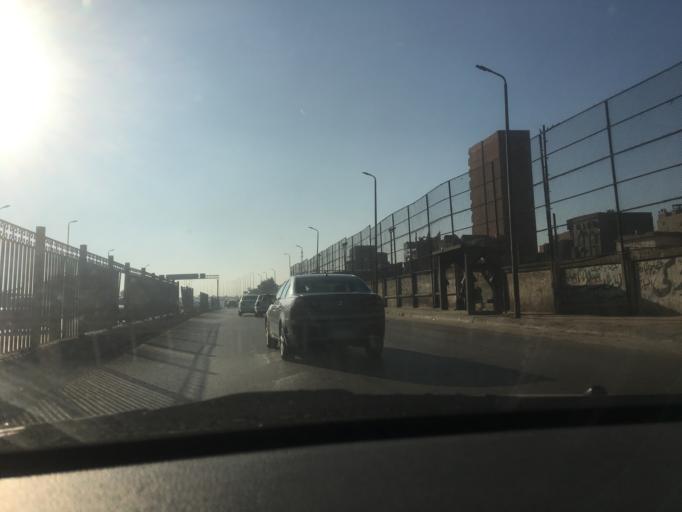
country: EG
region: Muhafazat al Qahirah
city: Cairo
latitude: 30.0133
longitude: 31.2668
